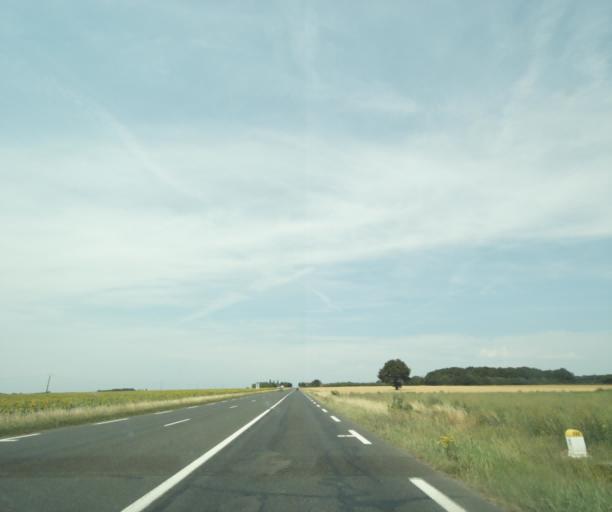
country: FR
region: Centre
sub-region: Departement d'Indre-et-Loire
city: Sainte-Maure-de-Touraine
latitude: 47.1653
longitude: 0.6507
